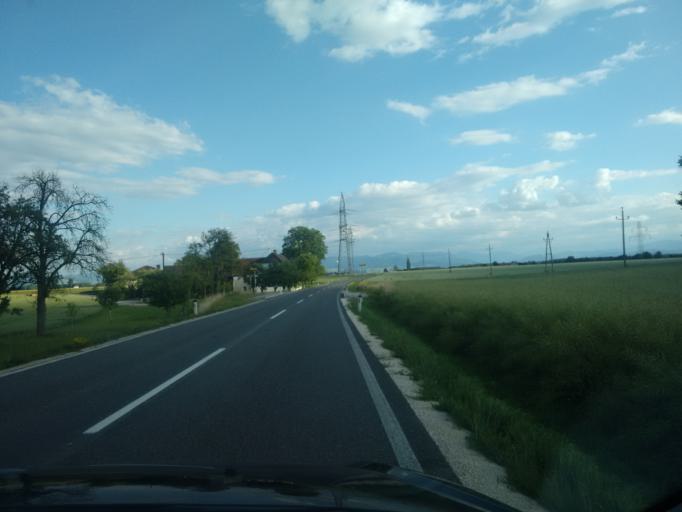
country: AT
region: Upper Austria
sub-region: Politischer Bezirk Steyr-Land
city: Sierning
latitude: 48.0945
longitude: 14.3189
